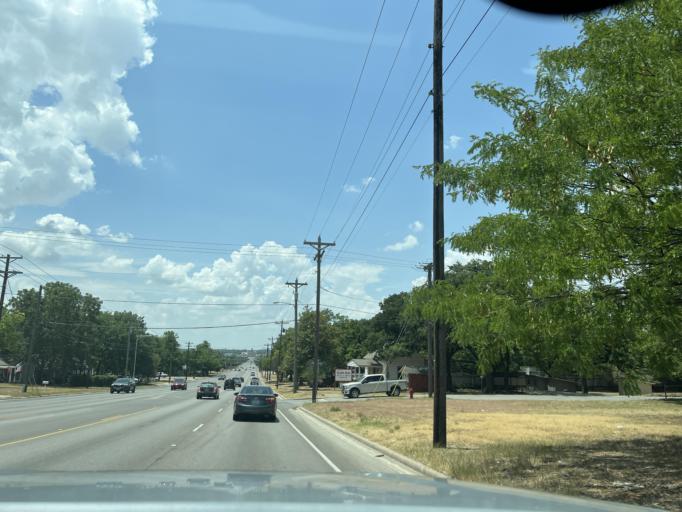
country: US
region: Texas
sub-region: Parker County
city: Weatherford
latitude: 32.7781
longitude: -97.7973
